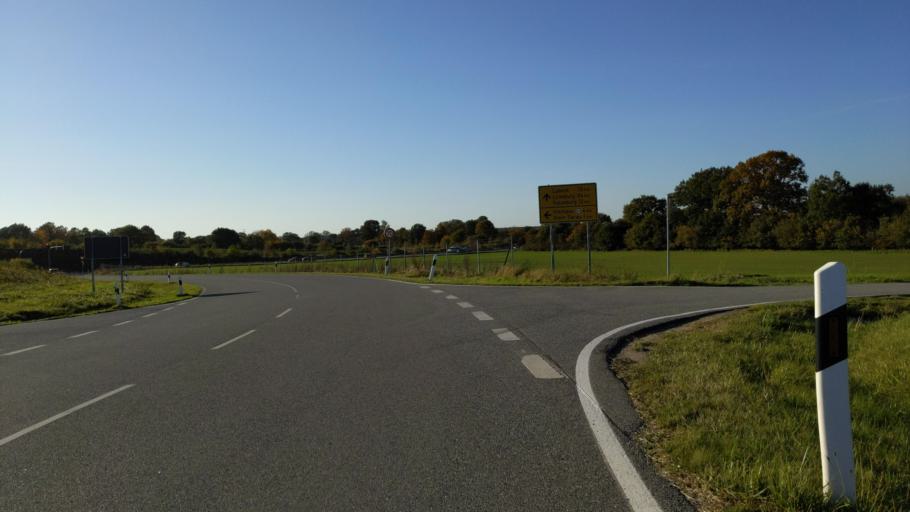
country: DE
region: Schleswig-Holstein
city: Gross Sarau
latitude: 53.7744
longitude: 10.7159
